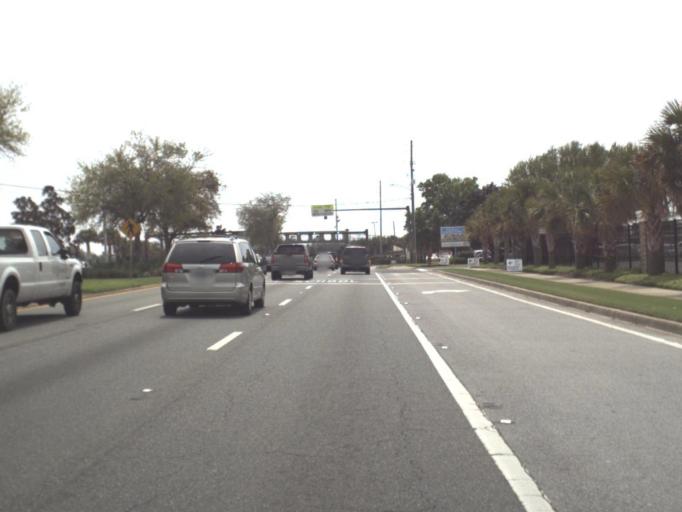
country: US
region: Florida
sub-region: Santa Rosa County
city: Gulf Breeze
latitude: 30.3620
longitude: -87.1687
